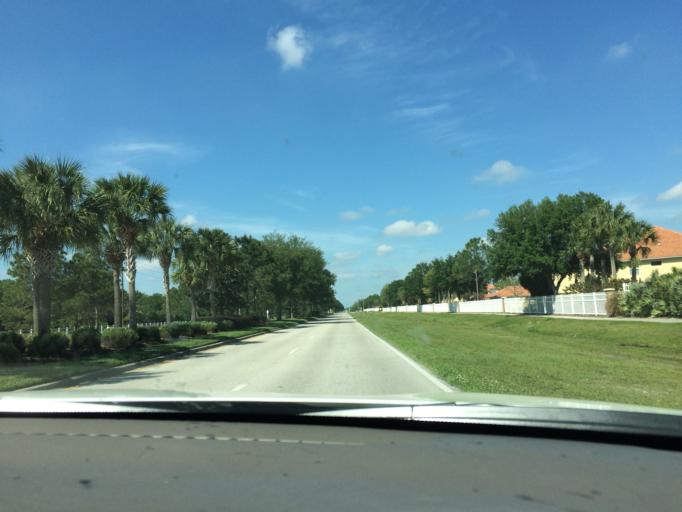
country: US
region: Florida
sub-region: Sarasota County
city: The Meadows
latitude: 27.3866
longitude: -82.4030
